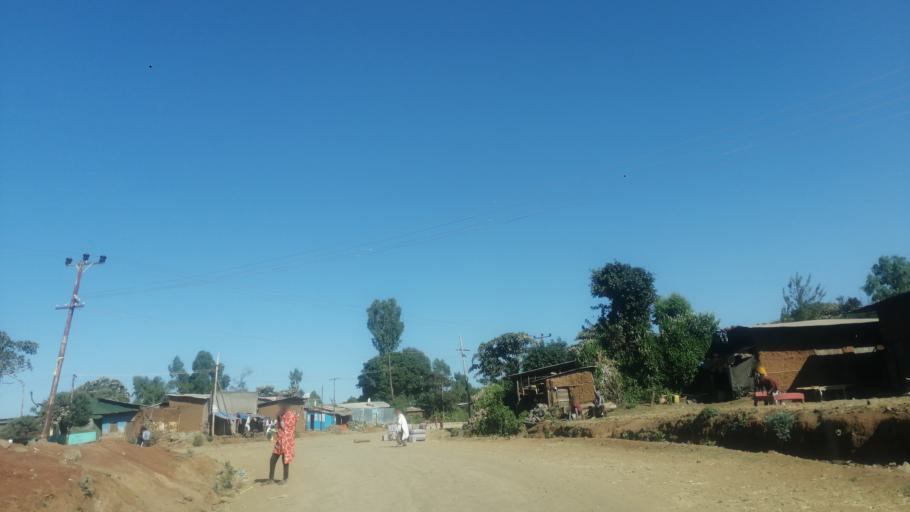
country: ET
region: Amhara
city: Addiet Canna
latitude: 11.0807
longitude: 37.8747
